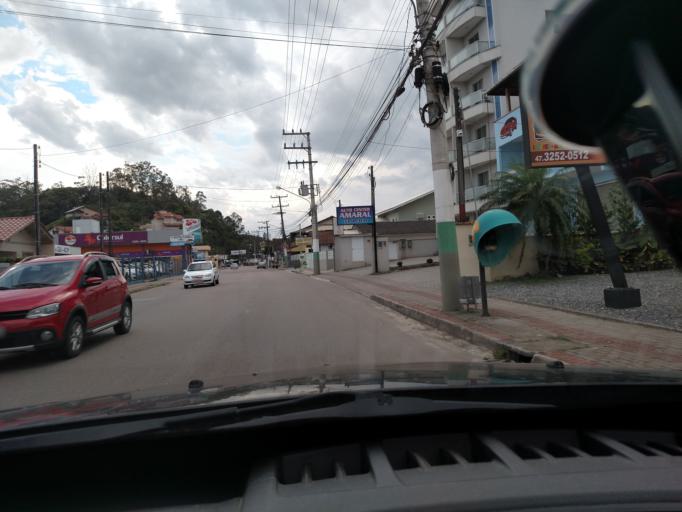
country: BR
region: Santa Catarina
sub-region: Brusque
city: Brusque
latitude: -27.0803
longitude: -48.8979
